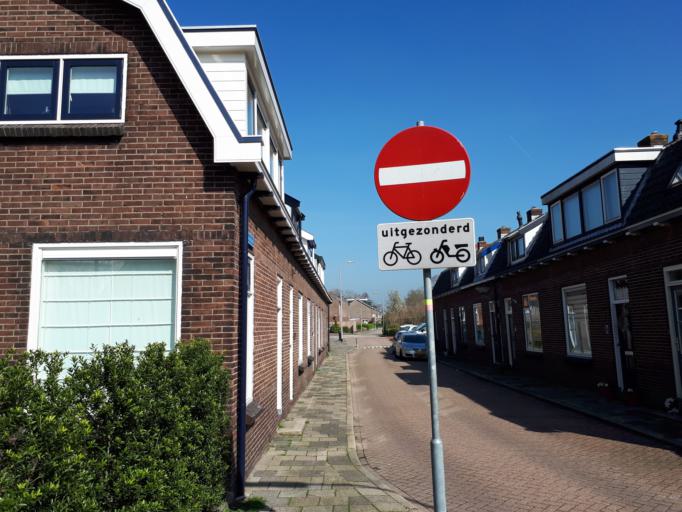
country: NL
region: South Holland
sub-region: Gemeente Krimpen aan den IJssel
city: Krimpen aan den IJssel
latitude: 51.9320
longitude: 4.6391
